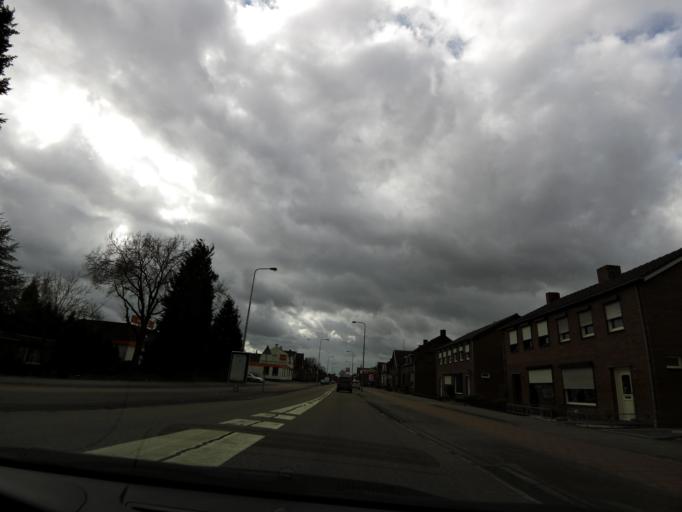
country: NL
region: Limburg
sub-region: Gemeente Beesel
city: Reuver
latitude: 51.2913
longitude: 6.0836
